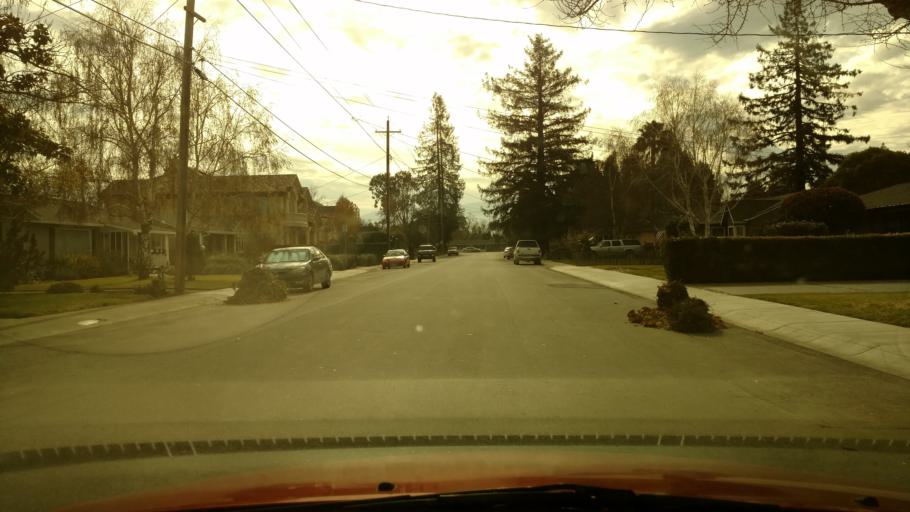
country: US
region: California
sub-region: Santa Clara County
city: Buena Vista
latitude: 37.2962
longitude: -121.9210
